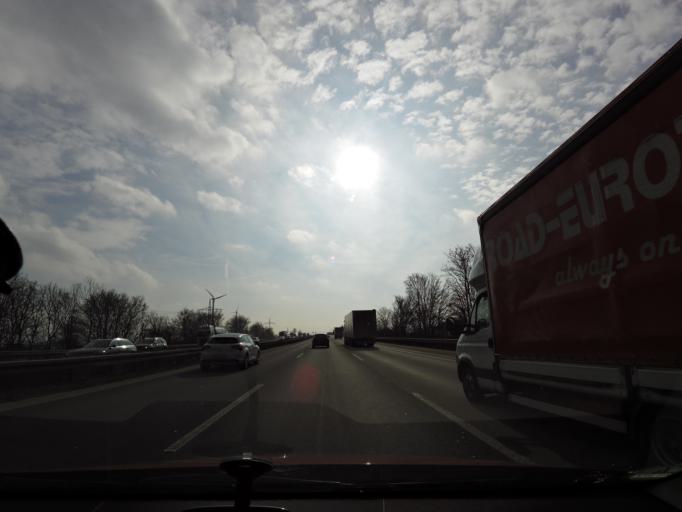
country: DE
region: Hesse
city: Bad Camberg
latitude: 50.2854
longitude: 8.2404
